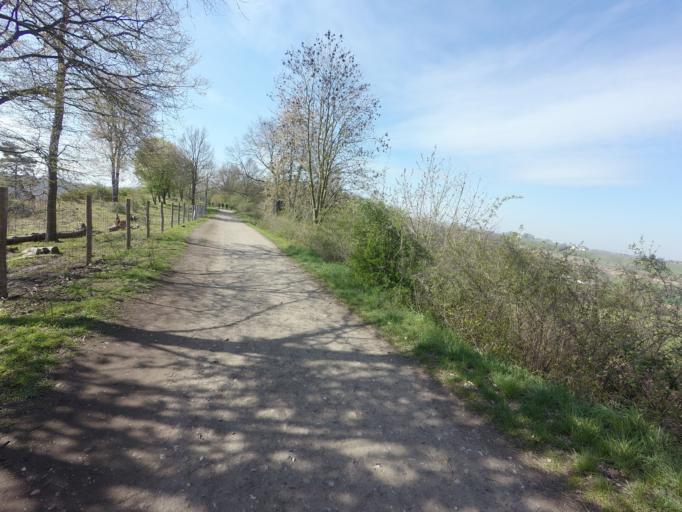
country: NL
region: Limburg
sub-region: Gemeente Maastricht
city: Maastricht
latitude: 50.8302
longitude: 5.6819
